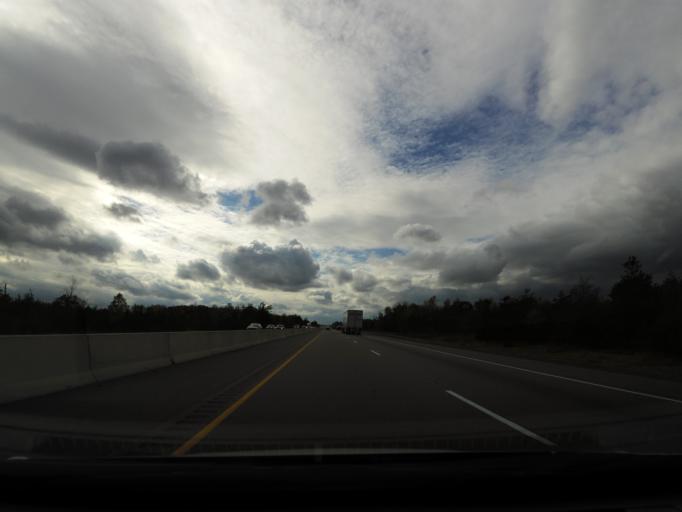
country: CA
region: Ontario
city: Deseronto
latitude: 44.2250
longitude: -77.2051
